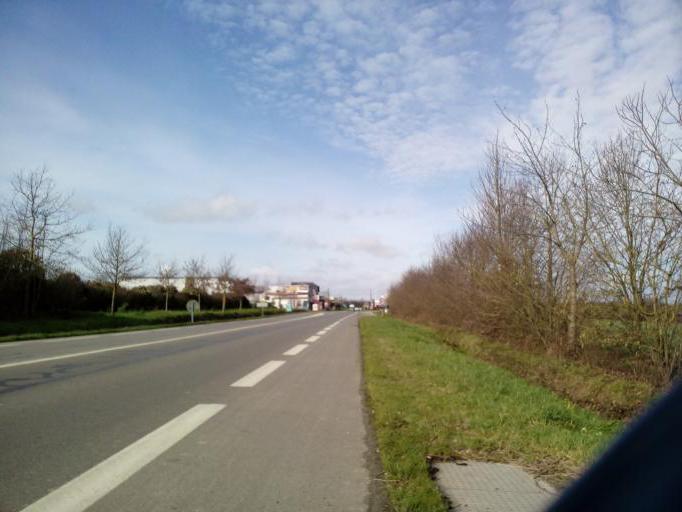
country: FR
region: Brittany
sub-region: Departement d'Ille-et-Vilaine
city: La Chapelle-des-Fougeretz
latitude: 48.1702
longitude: -1.7190
